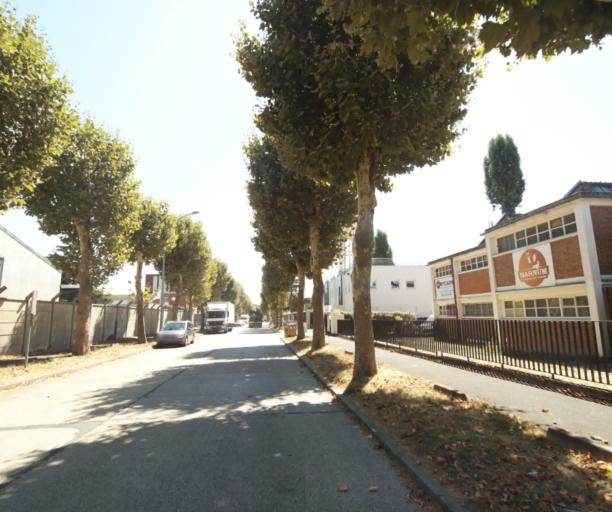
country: FR
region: Ile-de-France
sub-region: Departement des Hauts-de-Seine
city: Villeneuve-la-Garenne
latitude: 48.9455
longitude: 2.3192
